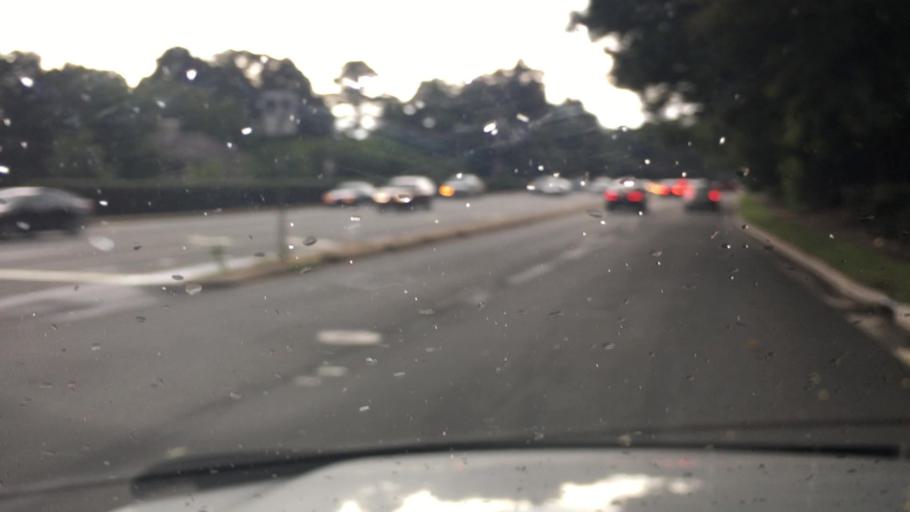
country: US
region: North Carolina
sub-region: Mecklenburg County
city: Matthews
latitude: 35.1544
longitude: -80.7952
